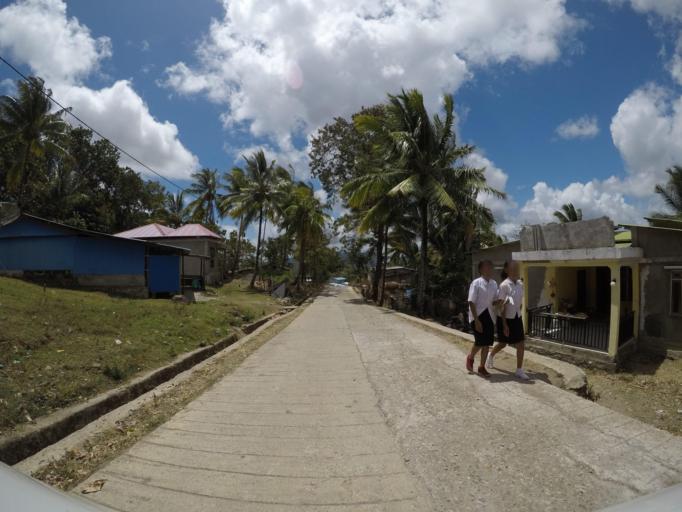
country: TL
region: Lautem
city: Lospalos
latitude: -8.5453
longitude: 126.8331
